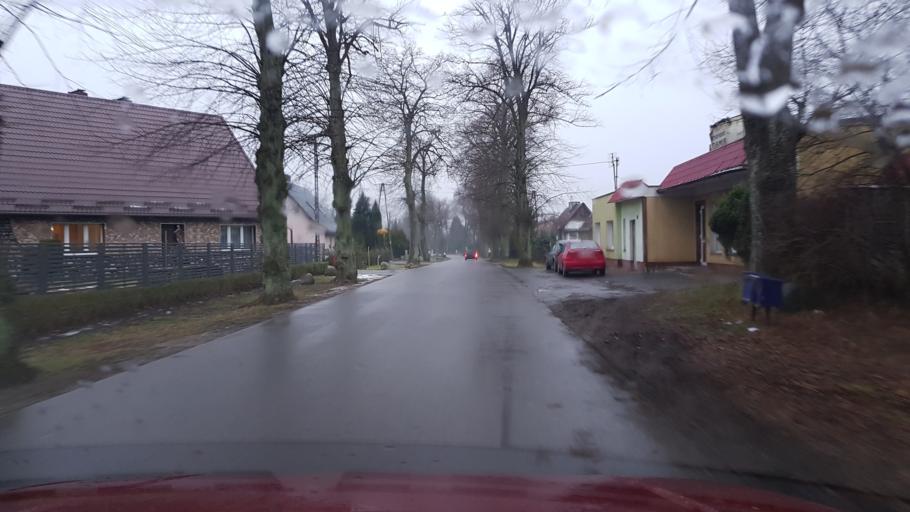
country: PL
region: West Pomeranian Voivodeship
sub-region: Powiat koszalinski
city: Sianow
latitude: 54.1757
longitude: 16.2492
